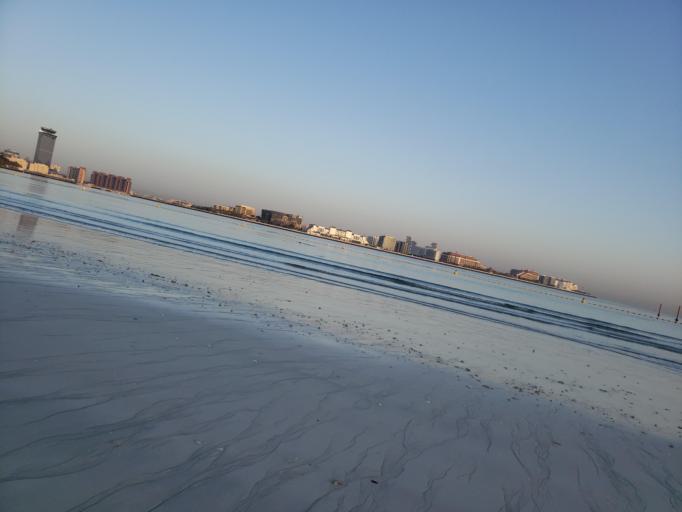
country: AE
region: Dubai
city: Dubai
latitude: 25.1196
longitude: 55.1695
